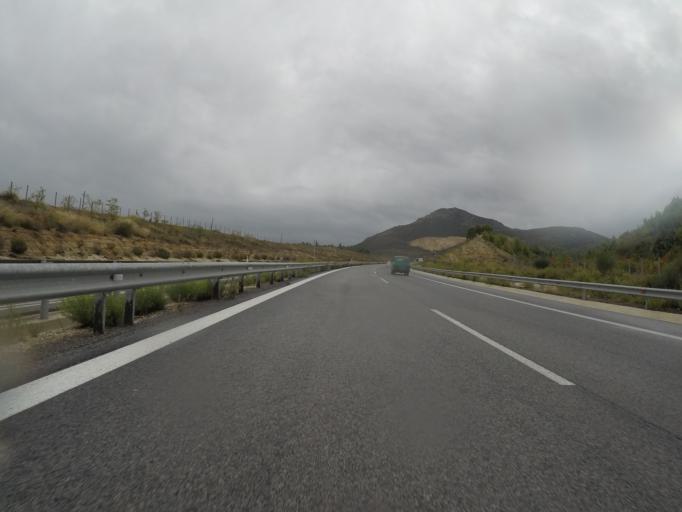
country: GR
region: Peloponnese
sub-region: Nomos Korinthias
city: Ayios Vasilios
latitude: 37.8461
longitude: 22.8171
